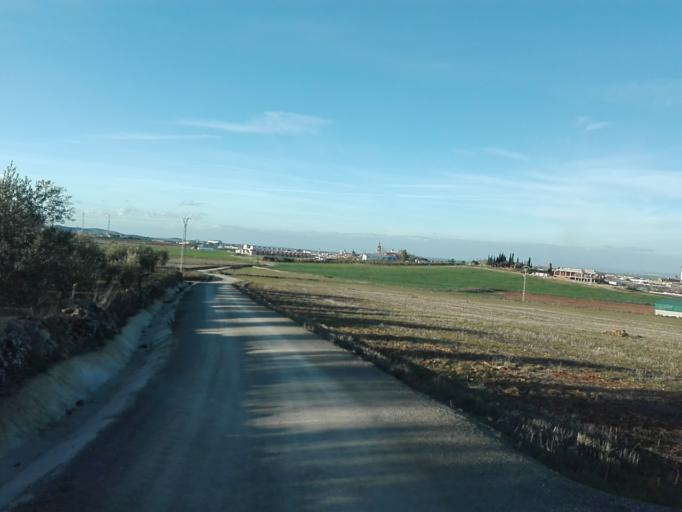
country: ES
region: Extremadura
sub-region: Provincia de Badajoz
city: Llerena
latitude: 38.2245
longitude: -6.0082
